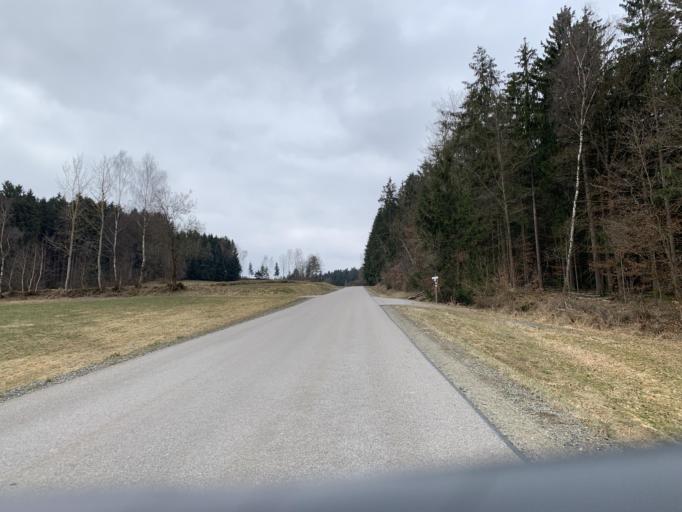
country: DE
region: Bavaria
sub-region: Upper Palatinate
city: Thanstein
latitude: 49.3875
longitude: 12.4528
